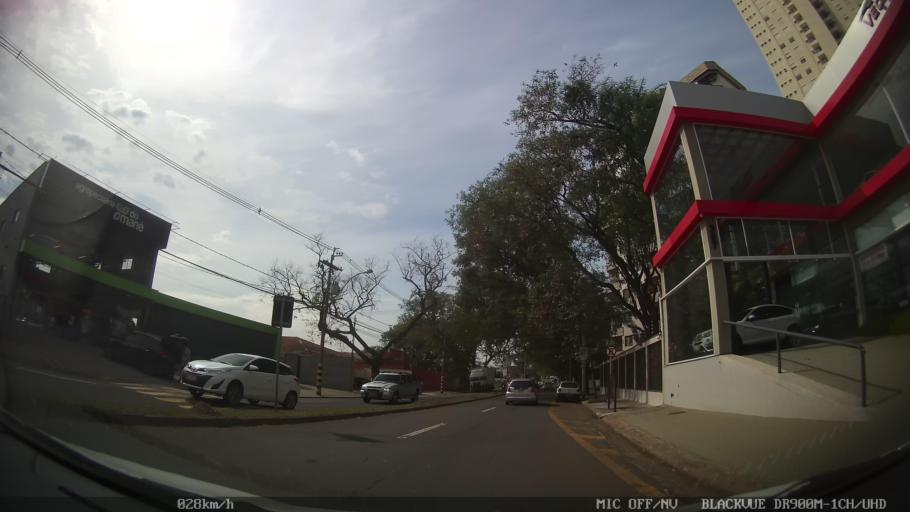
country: BR
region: Sao Paulo
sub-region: Piracicaba
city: Piracicaba
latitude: -22.7170
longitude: -47.6607
